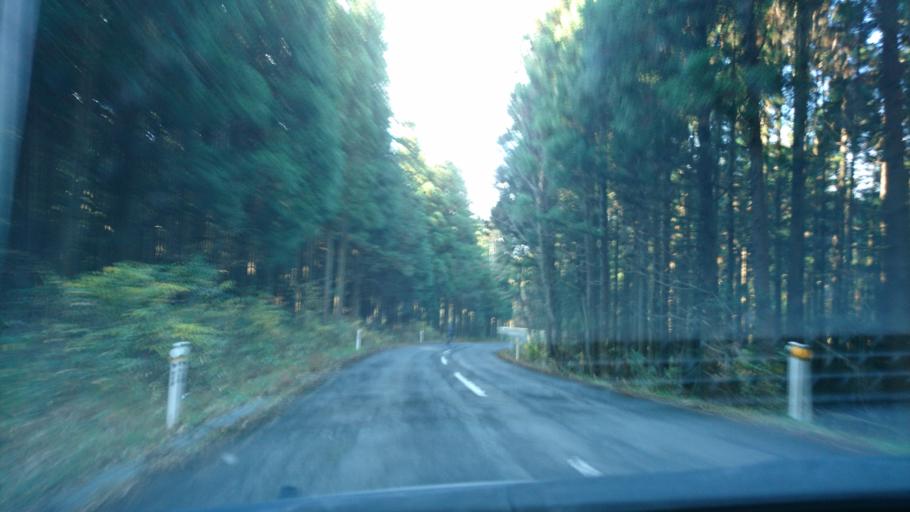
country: JP
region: Iwate
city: Mizusawa
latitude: 39.0325
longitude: 141.1592
